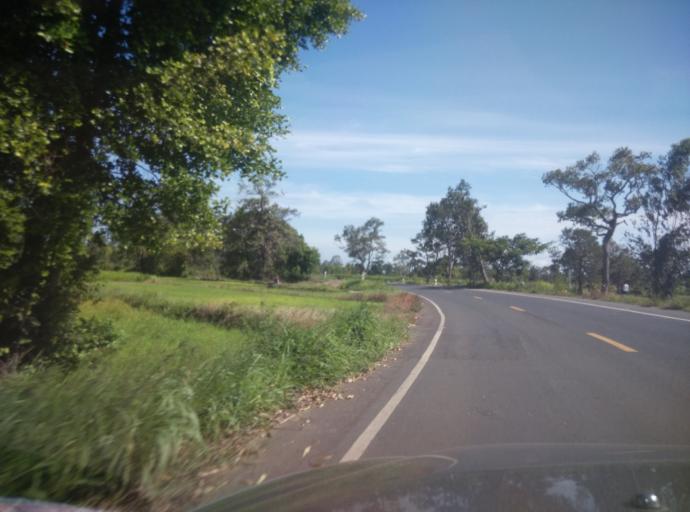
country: TH
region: Sisaket
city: Si Sa Ket
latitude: 15.1207
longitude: 104.2512
